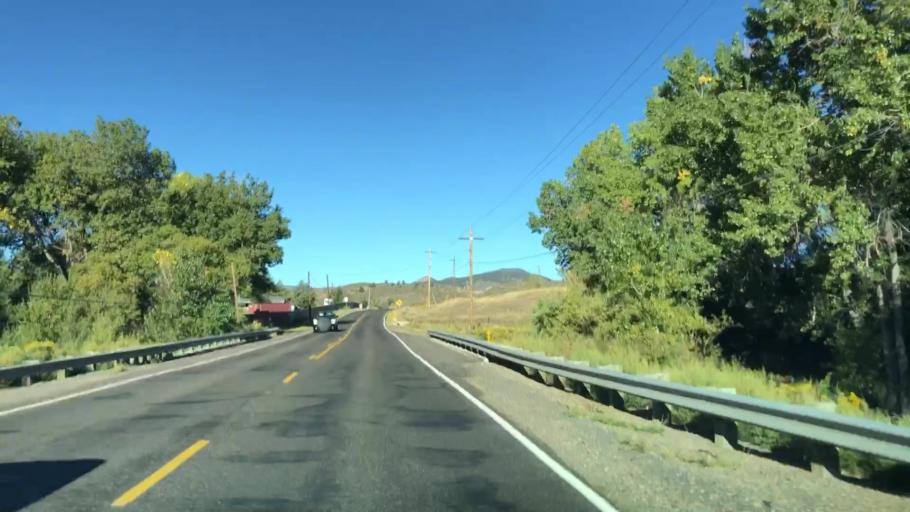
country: US
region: Colorado
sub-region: Larimer County
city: Loveland
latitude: 40.3932
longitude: -105.1655
